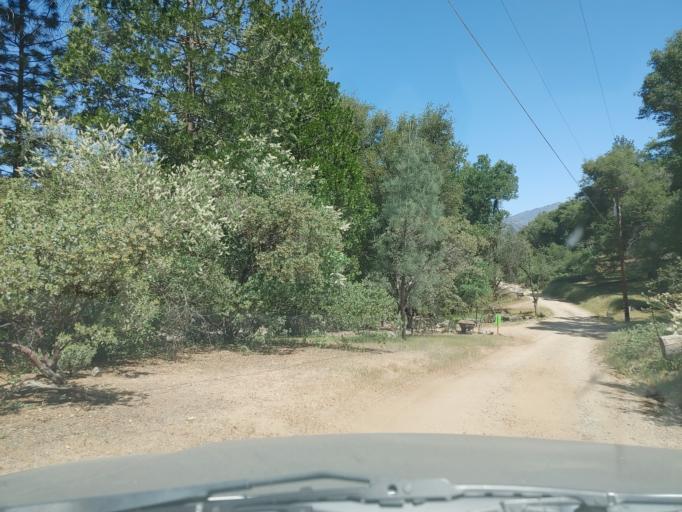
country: US
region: California
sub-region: Madera County
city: Oakhurst
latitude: 37.3215
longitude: -119.6380
